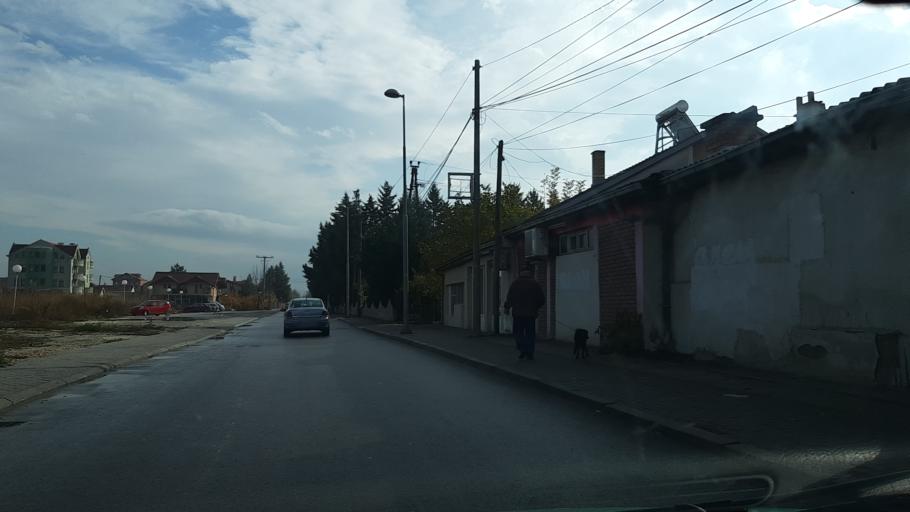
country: MK
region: Kisela Voda
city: Usje
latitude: 41.9795
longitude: 21.4806
